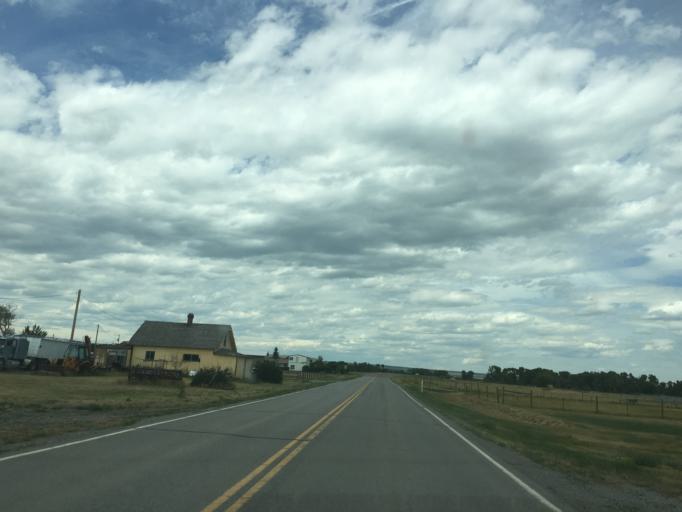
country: US
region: Montana
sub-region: Teton County
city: Choteau
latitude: 47.9789
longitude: -112.3126
